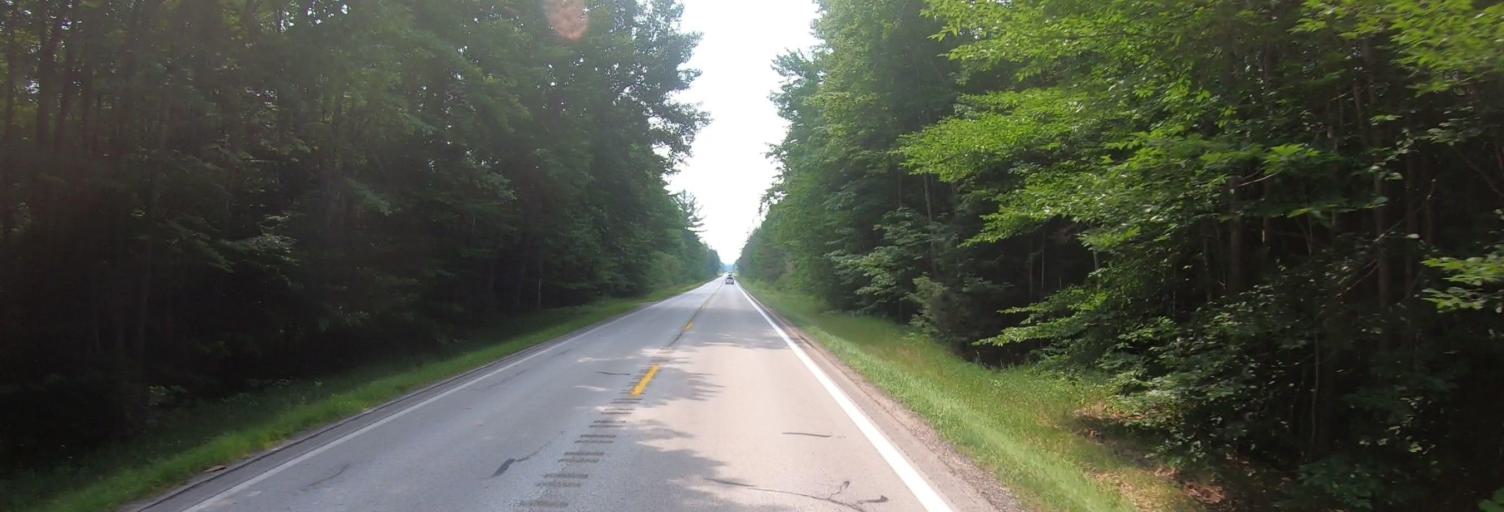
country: US
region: Michigan
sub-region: Luce County
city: Newberry
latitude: 46.4939
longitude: -85.4268
